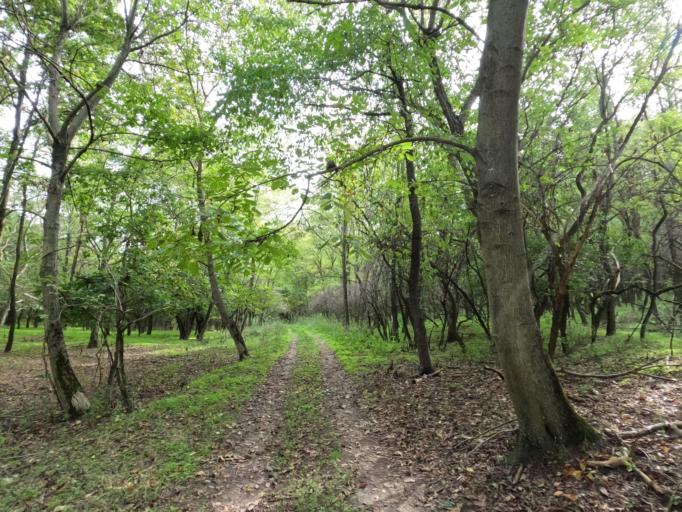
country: HU
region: Tolna
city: Szentgalpuszta
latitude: 46.3345
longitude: 18.6488
